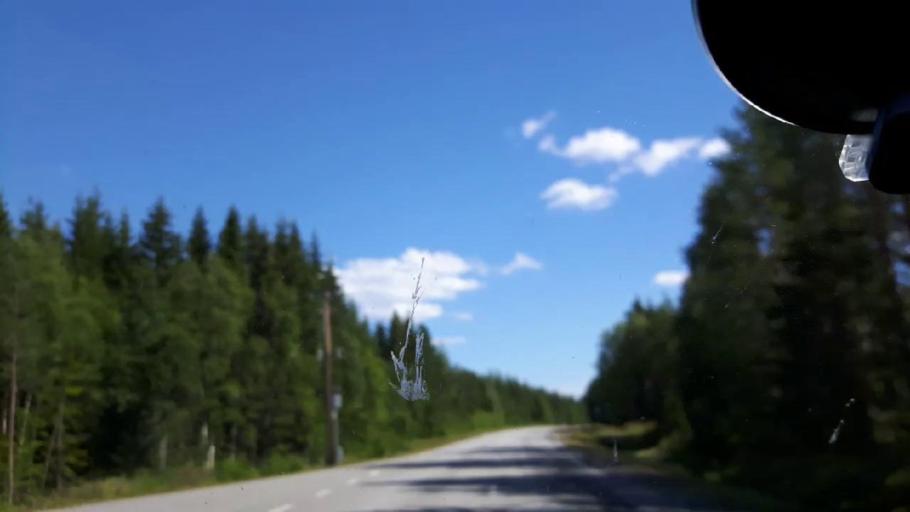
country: SE
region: Vaesternorrland
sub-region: Ange Kommun
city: Fransta
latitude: 62.7075
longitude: 16.3550
